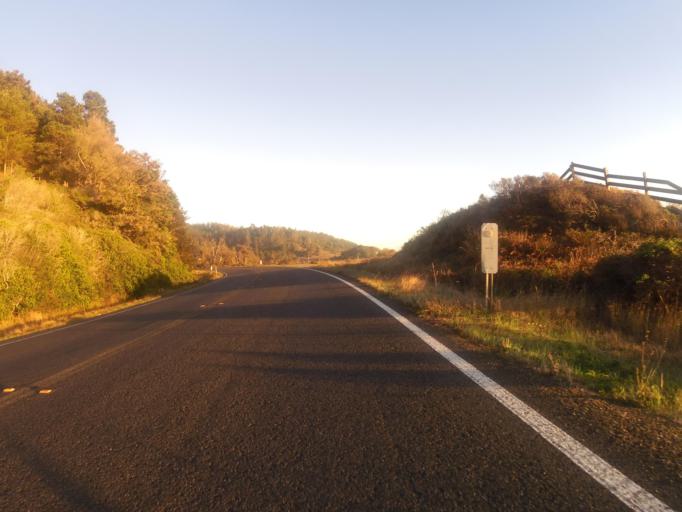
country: US
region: California
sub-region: Sonoma County
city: Sea Ranch
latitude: 38.6416
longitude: -123.3935
